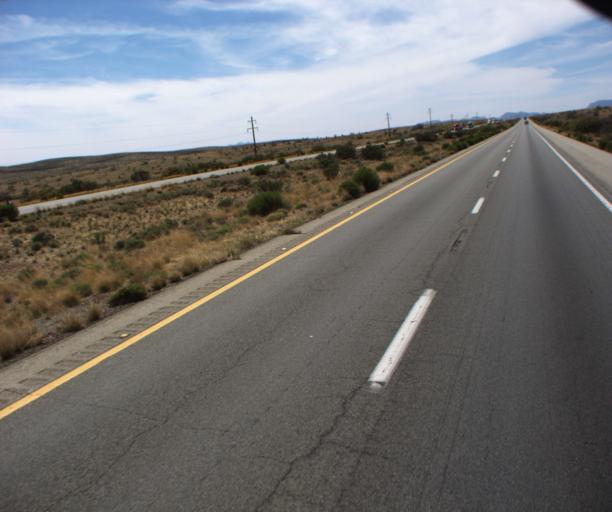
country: US
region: Arizona
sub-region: Cochise County
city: Willcox
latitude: 32.3518
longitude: -109.7262
